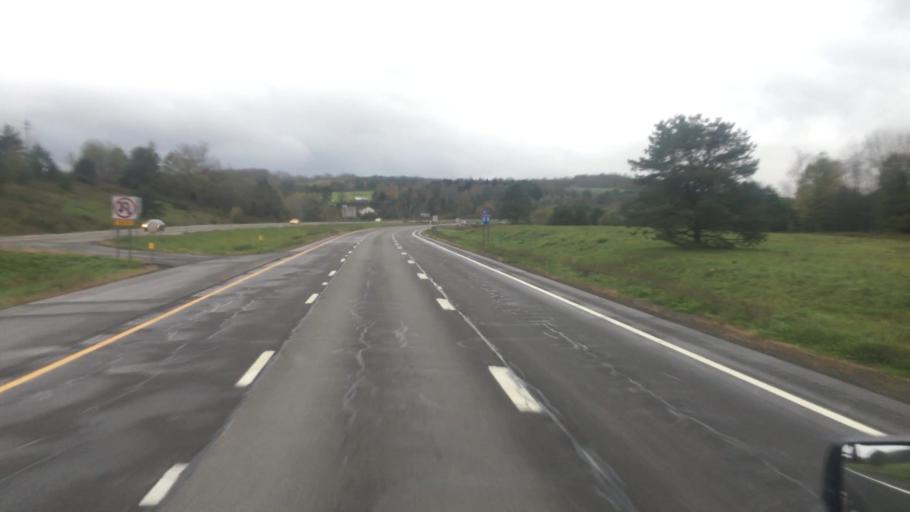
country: US
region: New York
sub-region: Chenango County
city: Greene
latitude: 42.1879
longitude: -75.6459
